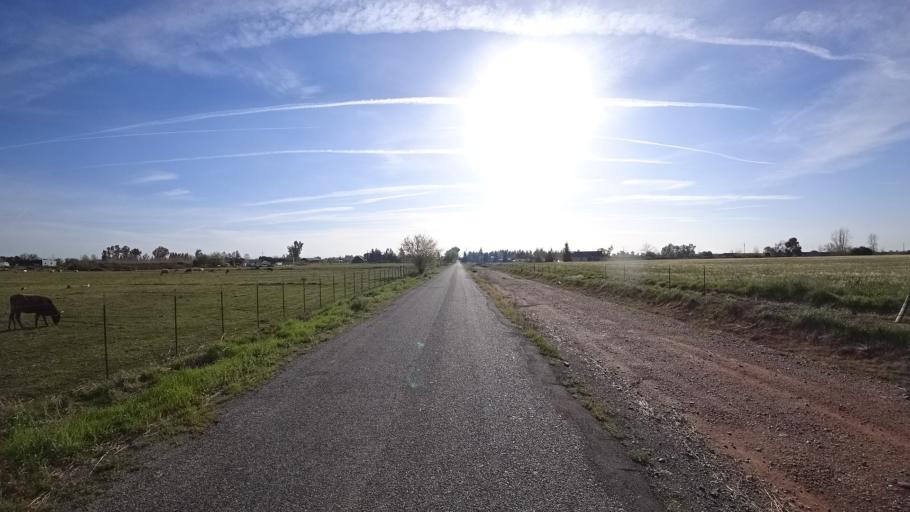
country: US
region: California
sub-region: Glenn County
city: Orland
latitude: 39.7154
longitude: -122.2317
